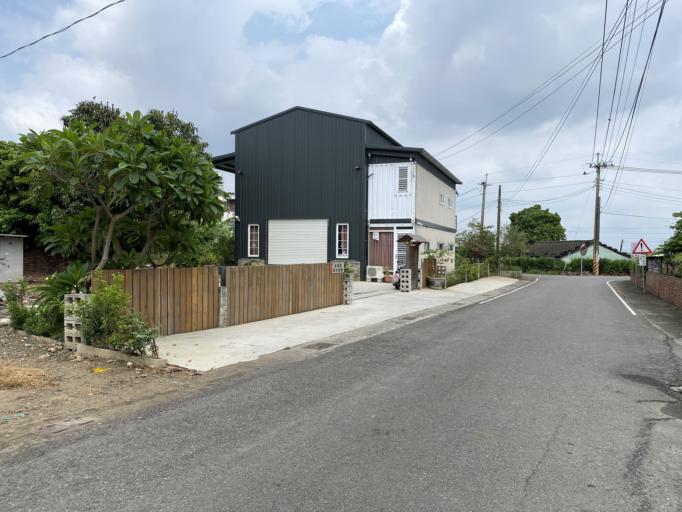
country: TW
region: Taiwan
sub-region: Chiayi
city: Jiayi Shi
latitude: 23.5791
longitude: 120.4190
